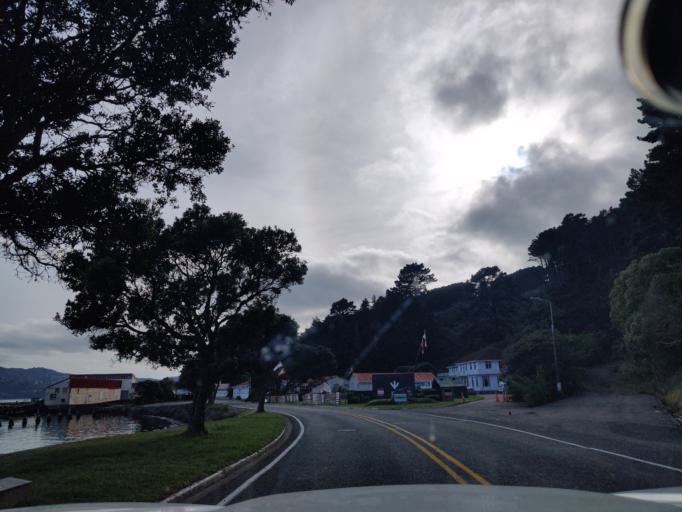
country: NZ
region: Wellington
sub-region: Wellington City
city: Wellington
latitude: -41.2964
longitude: 174.8223
